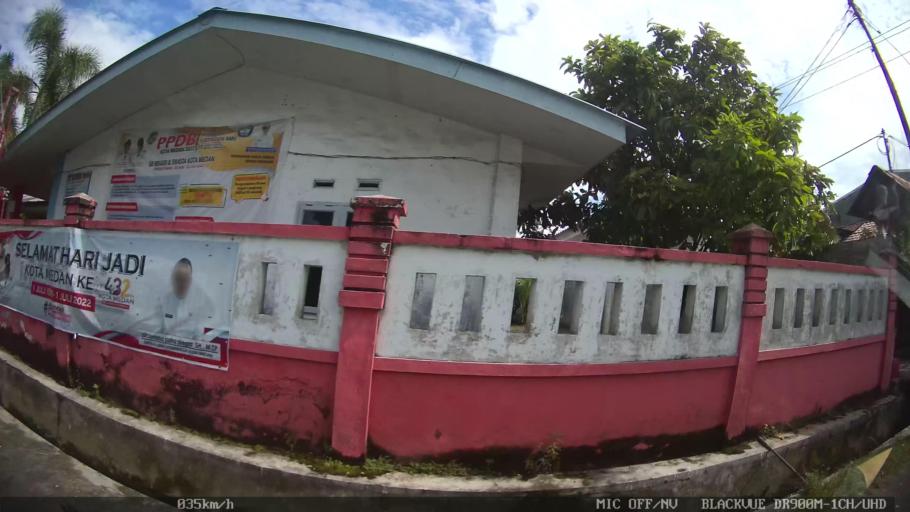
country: ID
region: North Sumatra
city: Sunggal
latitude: 3.6137
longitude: 98.6360
